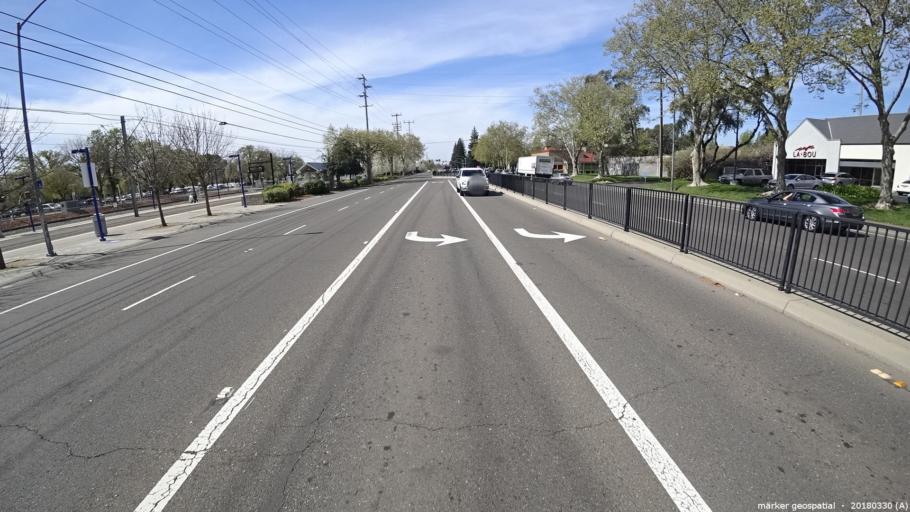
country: US
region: California
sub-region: Sacramento County
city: Rosemont
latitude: 38.5542
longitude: -121.3730
